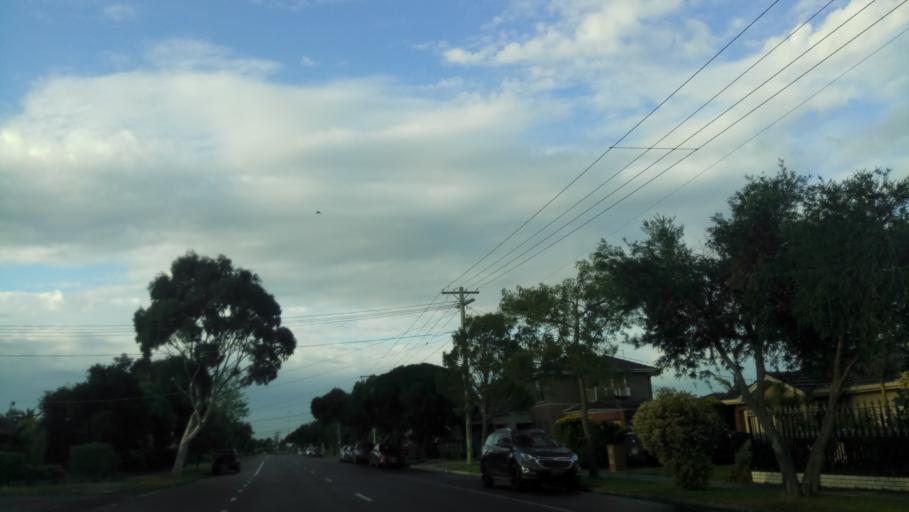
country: AU
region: Victoria
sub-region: Hobsons Bay
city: Altona Meadows
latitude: -37.8710
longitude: 144.7870
